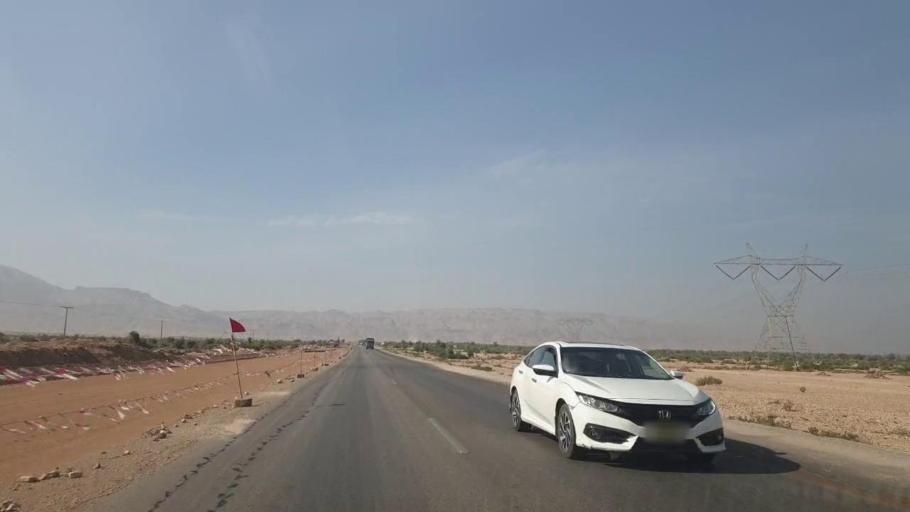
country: PK
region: Sindh
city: Sehwan
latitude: 26.2122
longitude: 67.9212
